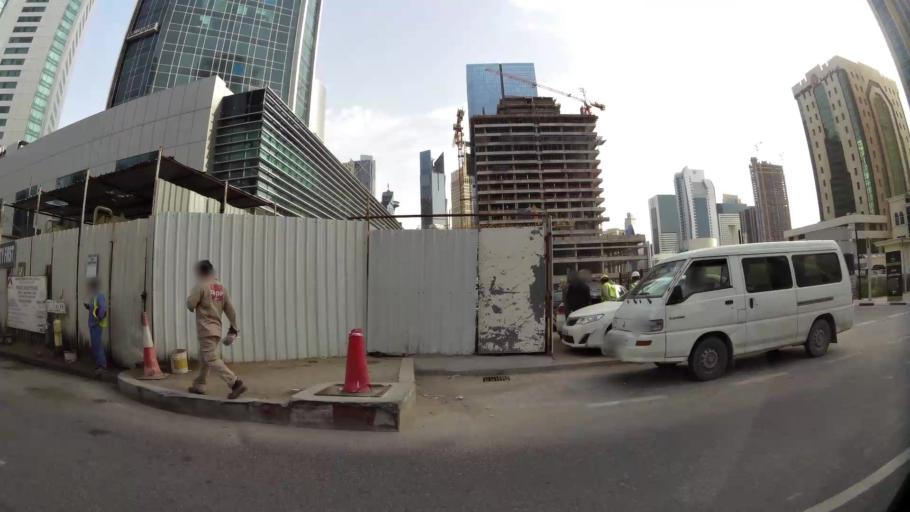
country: QA
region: Baladiyat ad Dawhah
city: Doha
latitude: 25.3248
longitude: 51.5256
